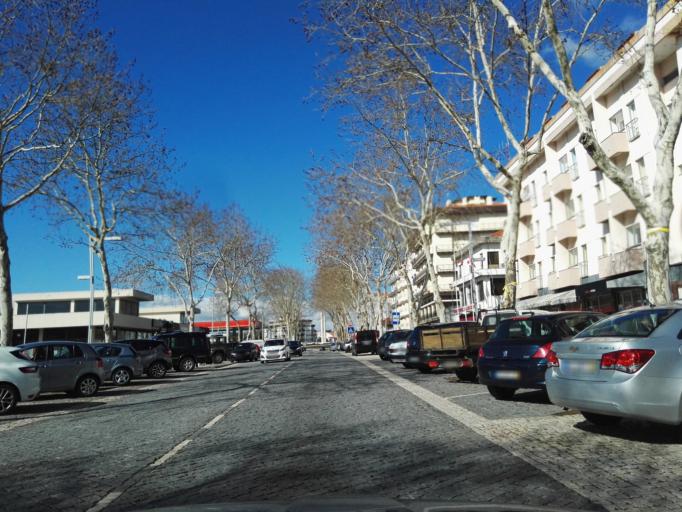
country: PT
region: Santarem
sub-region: Ourem
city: Fatima
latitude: 39.6328
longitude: -8.6815
